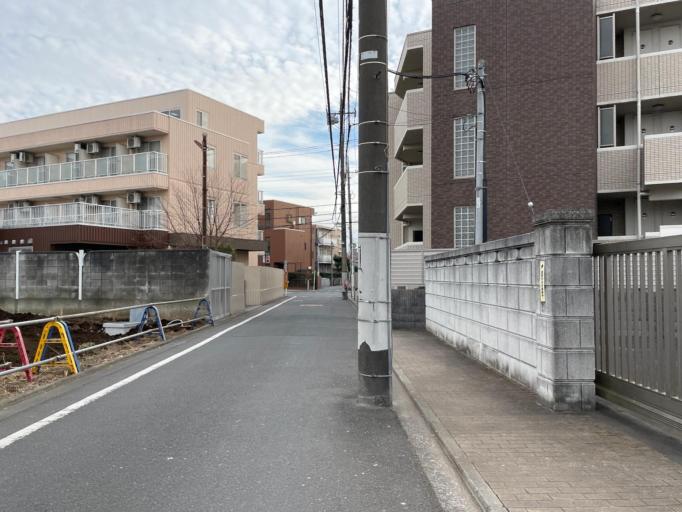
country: JP
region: Tokyo
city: Kamirenjaku
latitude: 35.7050
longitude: 139.5397
